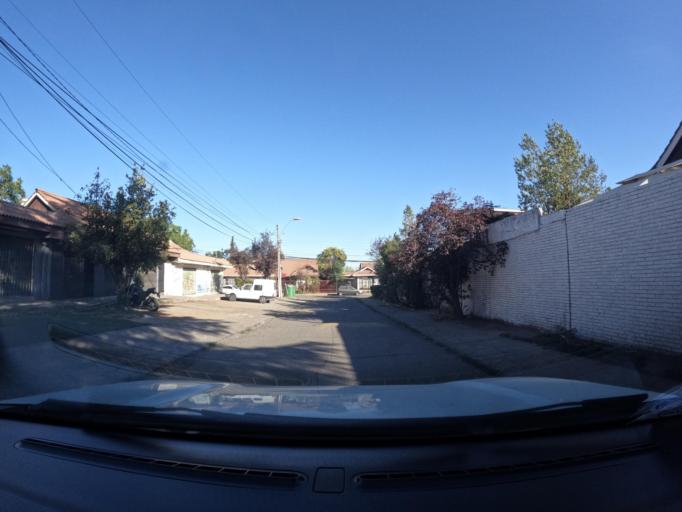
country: CL
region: Santiago Metropolitan
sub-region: Provincia de Santiago
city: Villa Presidente Frei, Nunoa, Santiago, Chile
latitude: -33.4776
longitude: -70.5547
